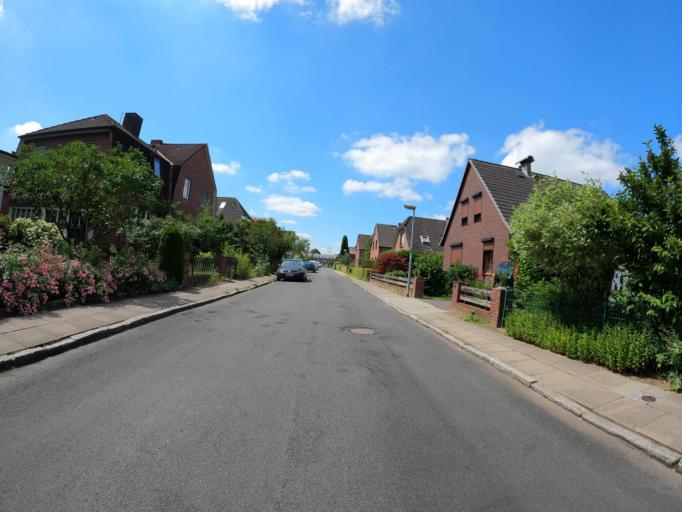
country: DE
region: Schleswig-Holstein
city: Wentorf bei Hamburg
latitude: 53.4931
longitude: 10.2597
